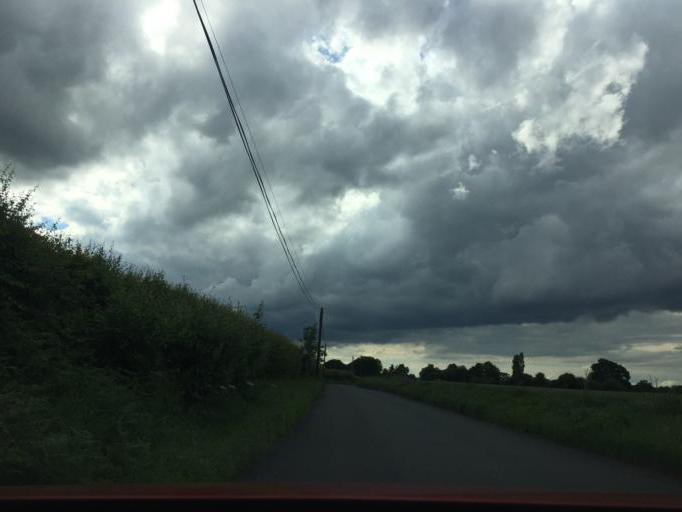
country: GB
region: England
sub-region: Hertfordshire
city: Harpenden
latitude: 51.8568
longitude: -0.3361
